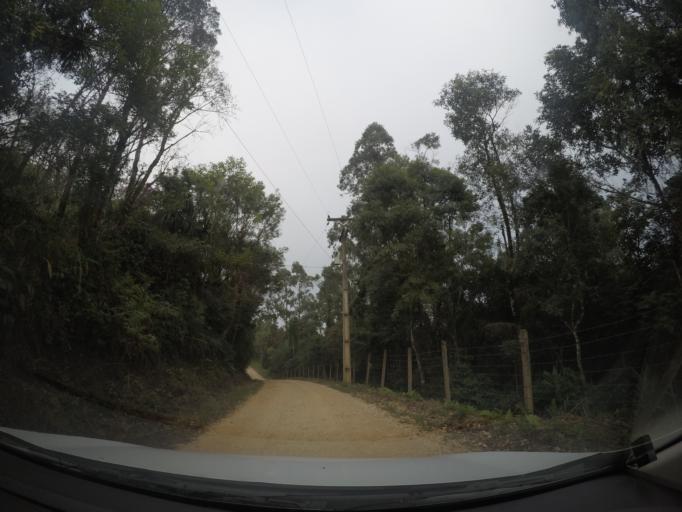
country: BR
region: Parana
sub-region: Colombo
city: Colombo
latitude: -25.3080
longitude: -49.2429
